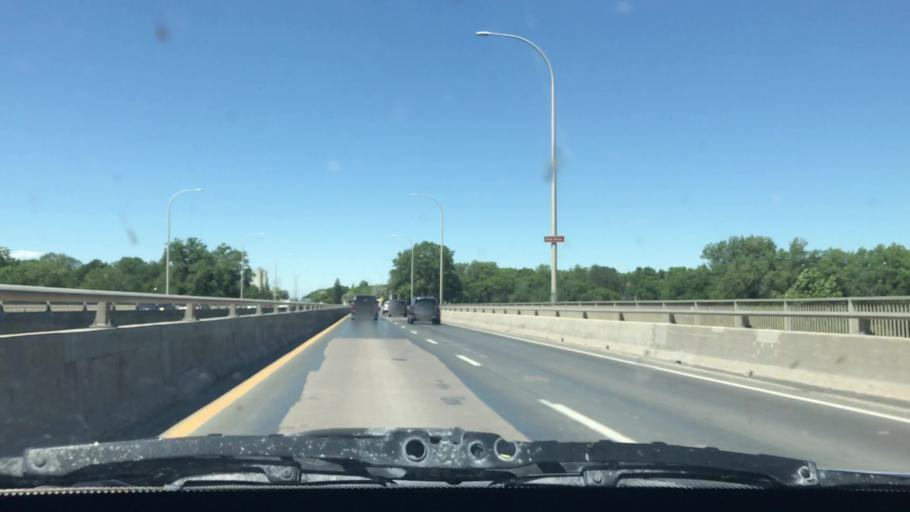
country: CA
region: Manitoba
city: Winnipeg
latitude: 49.8547
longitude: -97.1260
